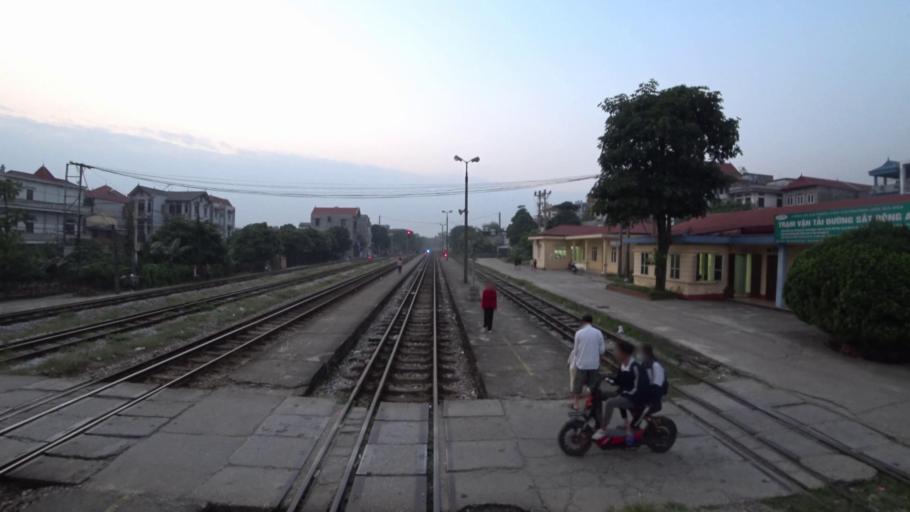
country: VN
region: Ha Noi
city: Soc Son
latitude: 21.2312
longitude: 105.8612
